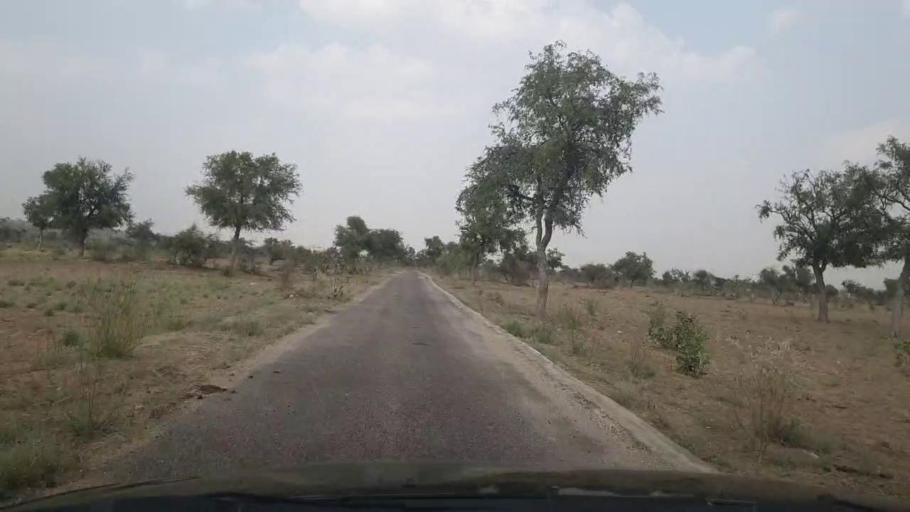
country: PK
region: Sindh
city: Islamkot
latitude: 24.9248
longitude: 70.5639
